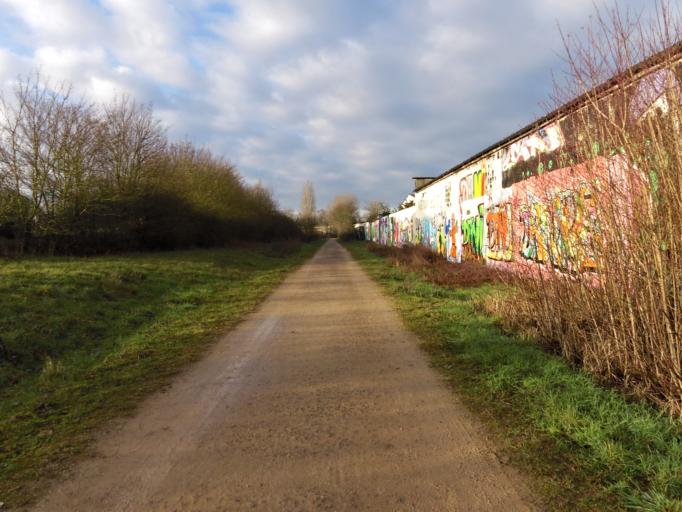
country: DE
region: Rheinland-Pfalz
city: Worms
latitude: 49.6107
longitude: 8.3424
